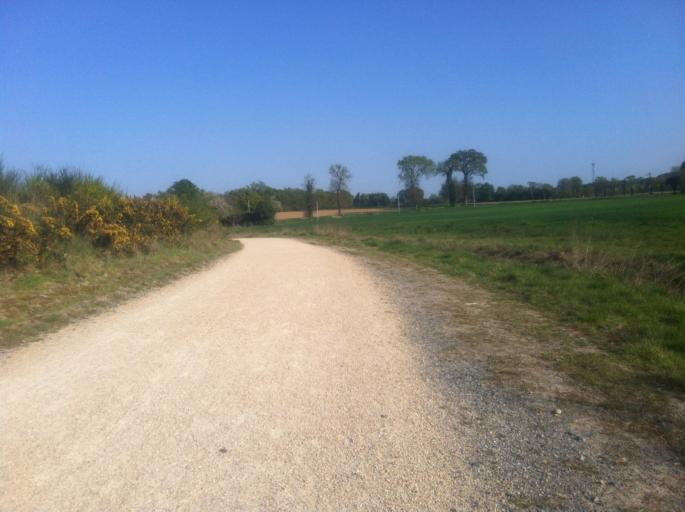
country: FR
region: Brittany
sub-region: Departement d'Ille-et-Vilaine
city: Chartres-de-Bretagne
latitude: 48.0116
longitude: -1.7152
